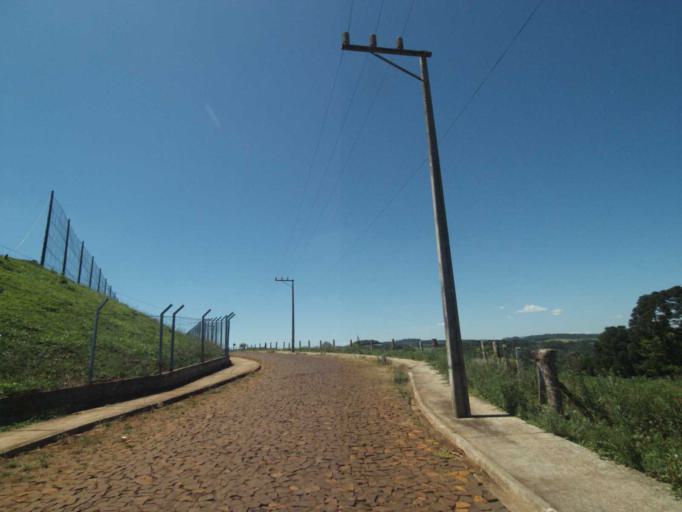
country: BR
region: Parana
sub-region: Laranjeiras Do Sul
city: Laranjeiras do Sul
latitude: -25.3854
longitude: -52.2105
